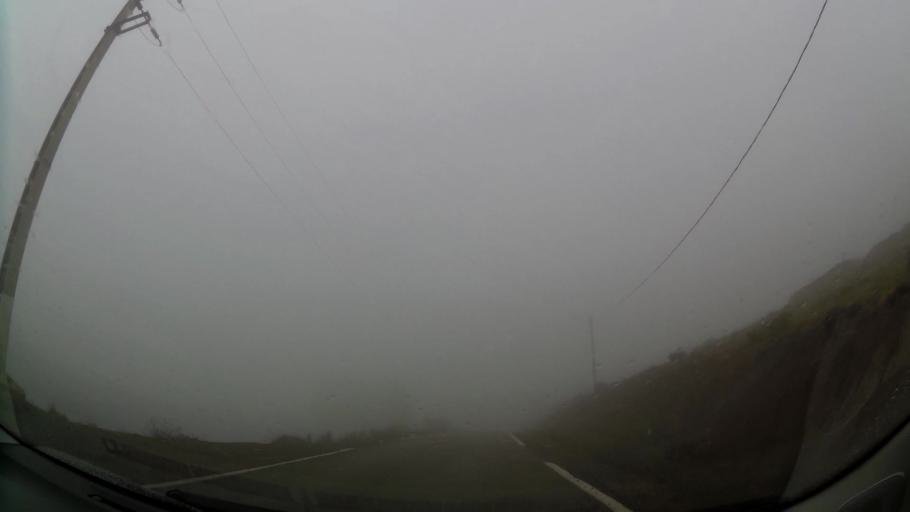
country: MA
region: Taza-Al Hoceima-Taounate
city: Tirhanimine
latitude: 35.2328
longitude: -3.9701
